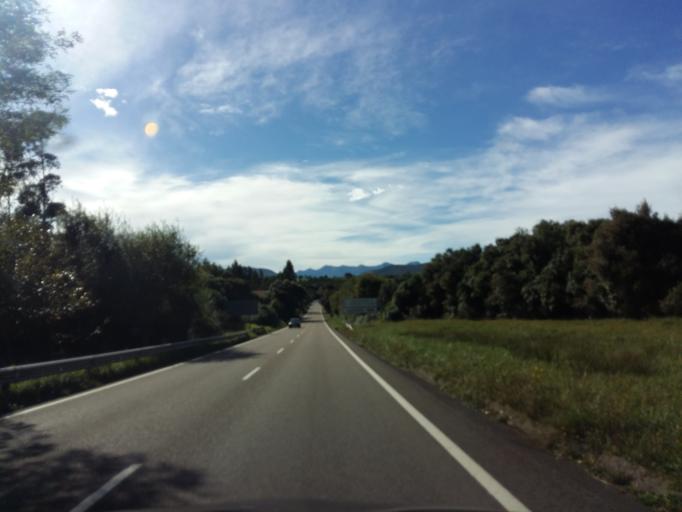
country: ES
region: Cantabria
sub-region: Provincia de Cantabria
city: San Vicente de la Barquera
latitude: 43.3404
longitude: -4.4876
